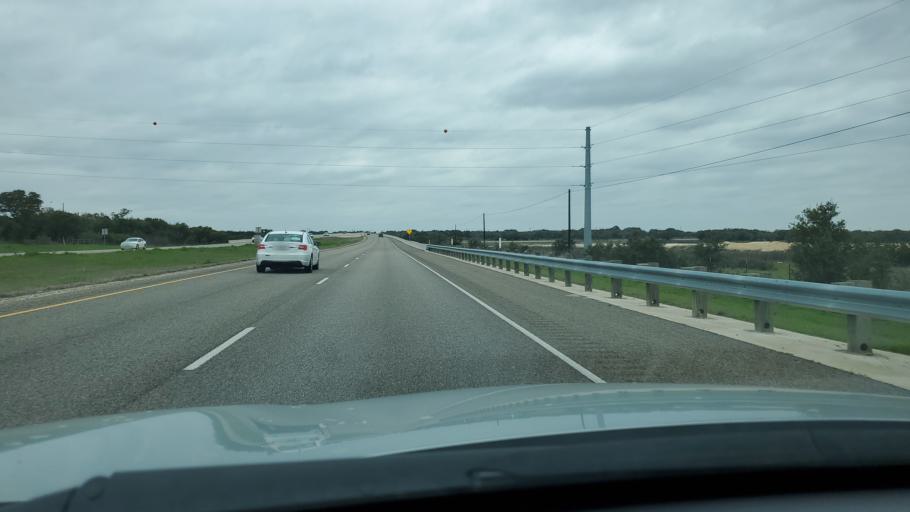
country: US
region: Texas
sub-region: Williamson County
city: Serenada
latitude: 30.7526
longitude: -97.7153
